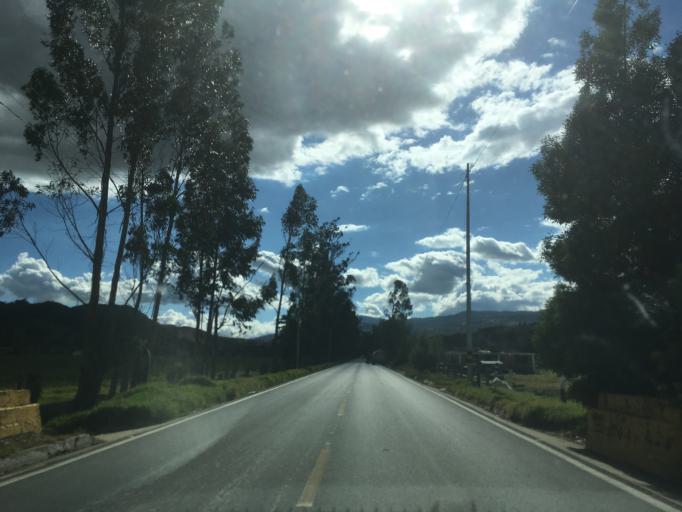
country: CO
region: Boyaca
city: Firavitoba
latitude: 5.6406
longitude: -72.9930
